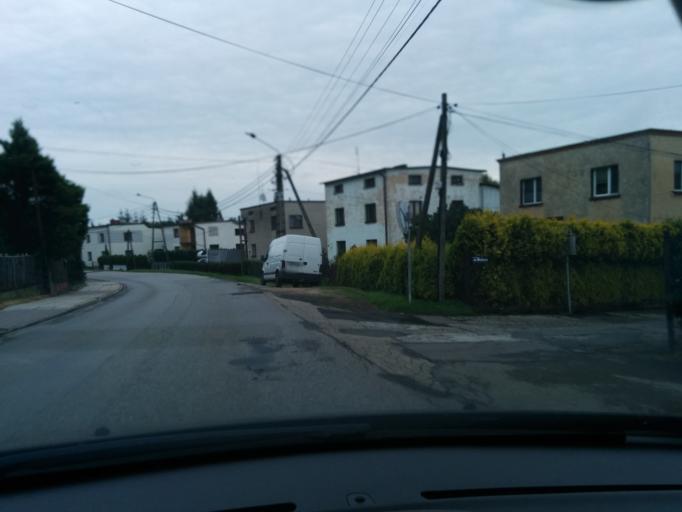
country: PL
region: Silesian Voivodeship
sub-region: Powiat bielski
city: Bujakow
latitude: 49.8737
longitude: 19.1970
